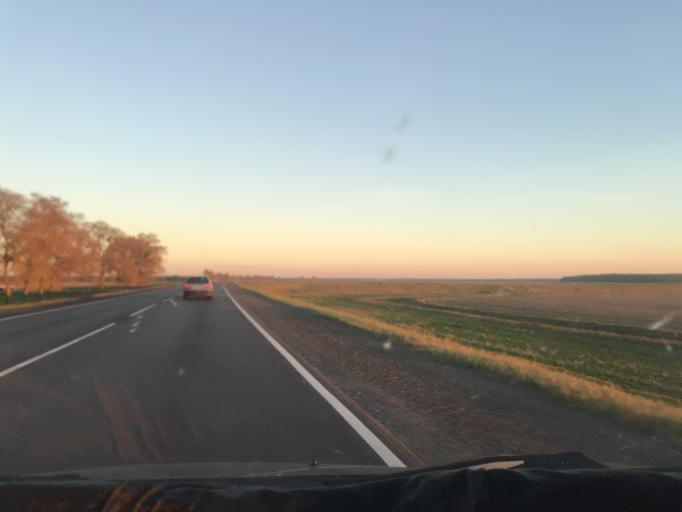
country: BY
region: Gomel
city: Kalinkavichy
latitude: 52.1655
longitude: 29.2216
